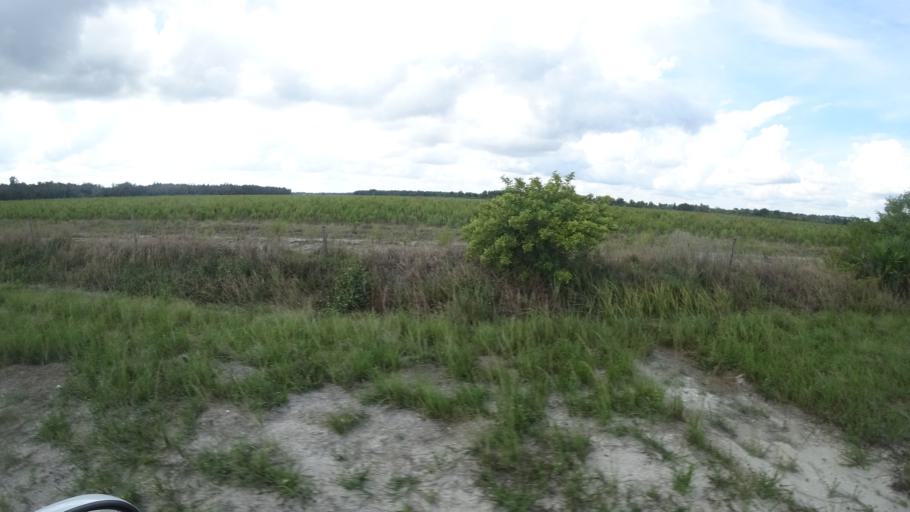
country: US
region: Florida
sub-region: Hillsborough County
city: Wimauma
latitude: 27.5770
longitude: -82.1740
